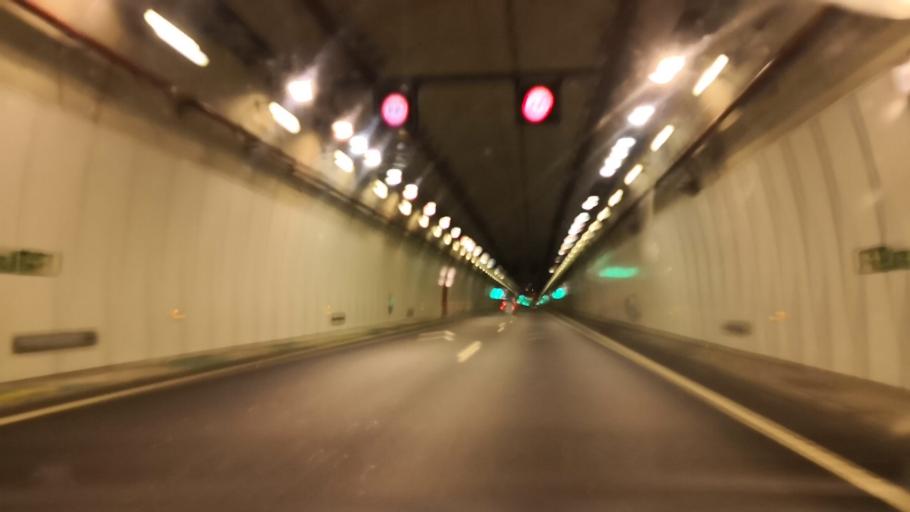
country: ES
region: Galicia
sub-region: Provincia de Pontevedra
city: Covelo
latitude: 42.1748
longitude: -8.3670
